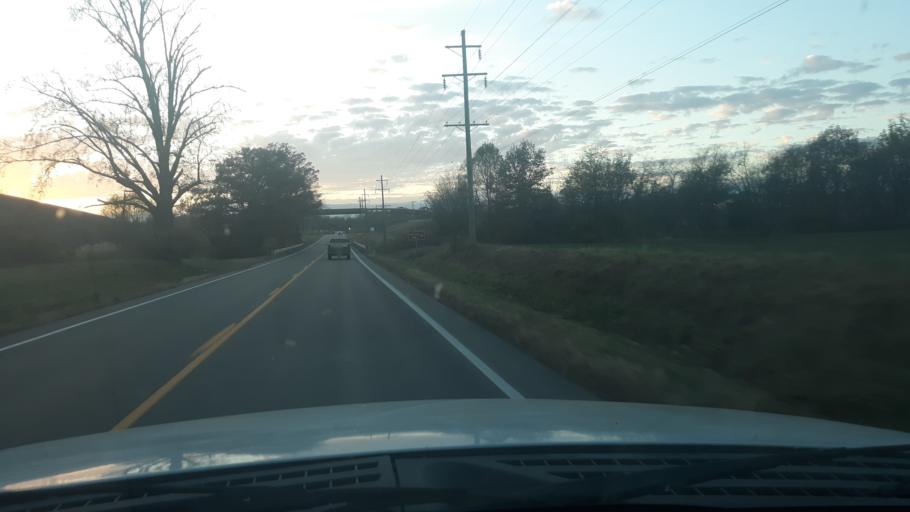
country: US
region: Illinois
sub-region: Saline County
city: Harrisburg
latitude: 37.8347
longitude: -88.5780
